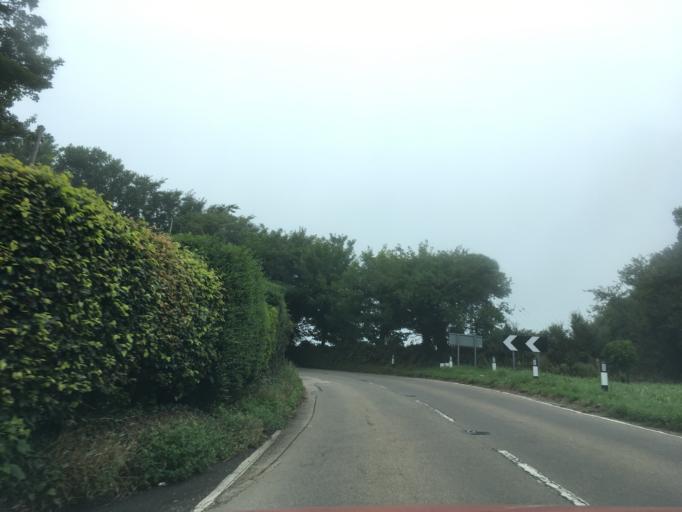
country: GB
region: Wales
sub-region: Pembrokeshire
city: Saint David's
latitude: 51.8792
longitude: -5.2162
